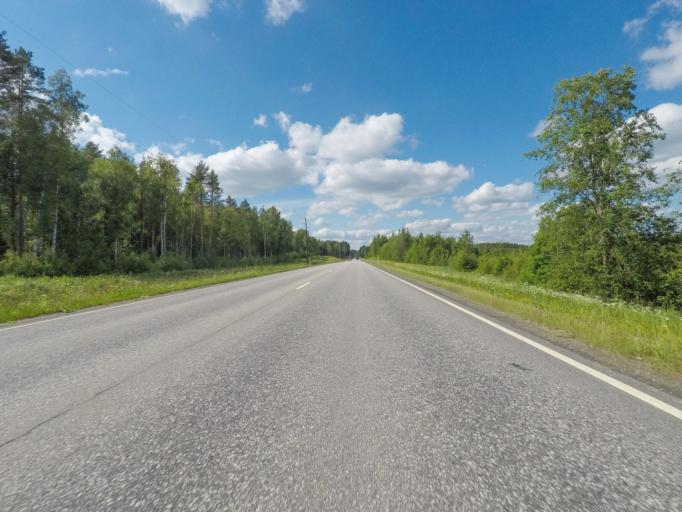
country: FI
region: Southern Savonia
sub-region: Savonlinna
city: Kerimaeki
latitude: 61.8737
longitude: 29.1196
